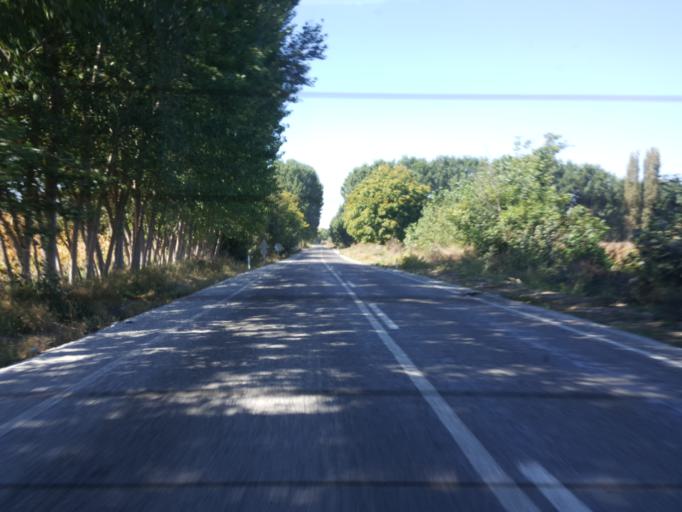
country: TR
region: Tokat
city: Pazar
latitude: 40.2698
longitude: 36.2322
